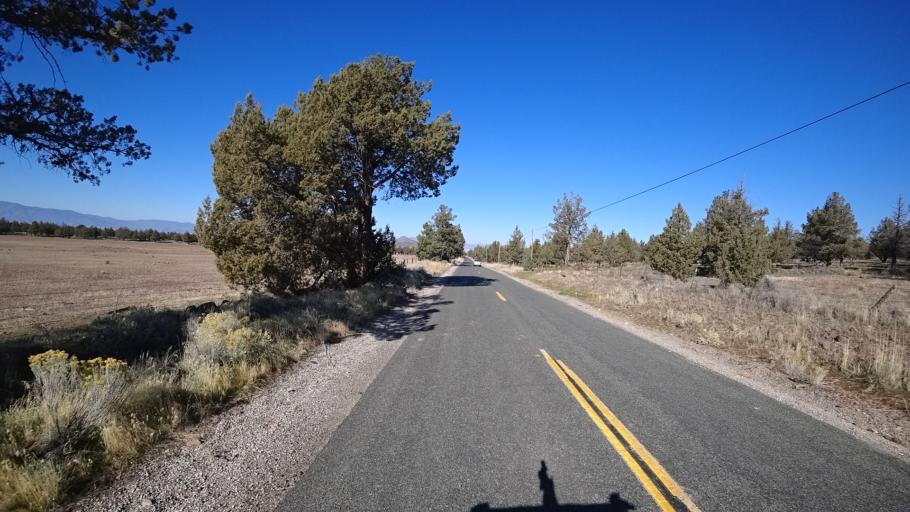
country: US
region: California
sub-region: Siskiyou County
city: Weed
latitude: 41.6304
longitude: -122.3341
